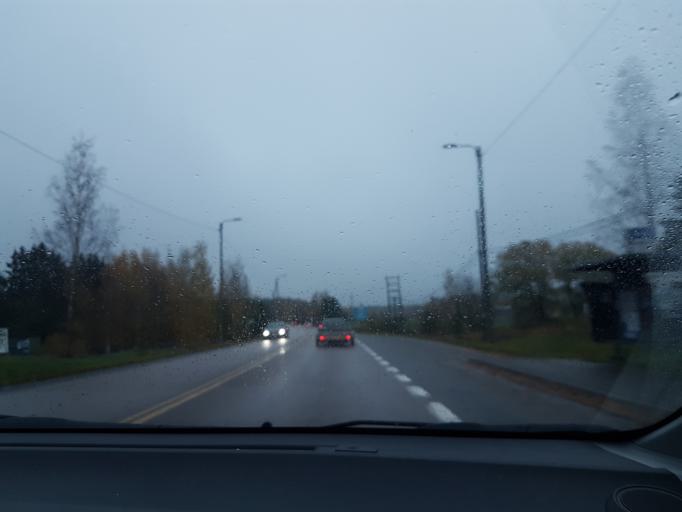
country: FI
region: Uusimaa
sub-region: Helsinki
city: Tuusula
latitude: 60.4153
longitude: 25.0515
